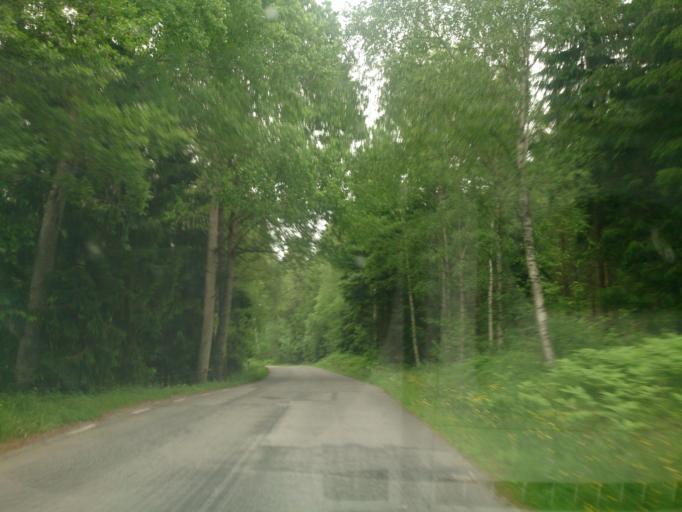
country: SE
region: OEstergoetland
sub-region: Soderkopings Kommun
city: Soederkoeping
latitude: 58.3193
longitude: 16.2911
